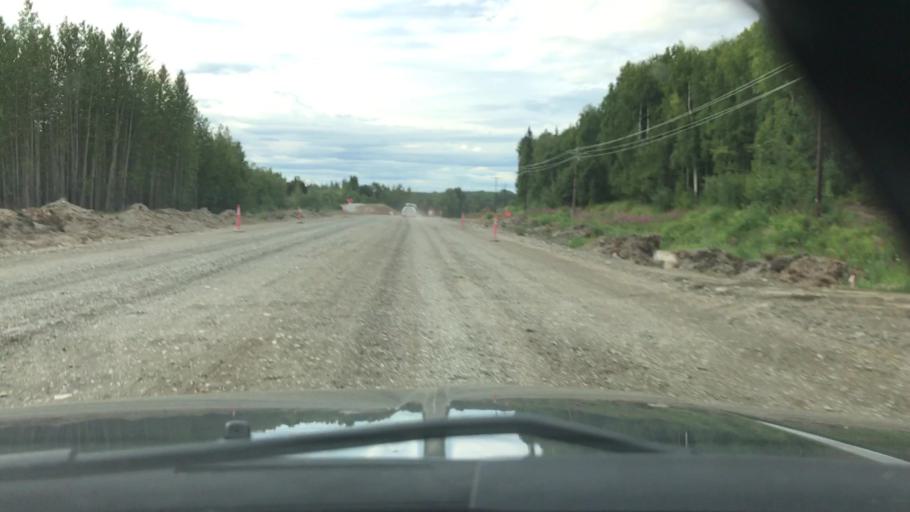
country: US
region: Alaska
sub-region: Matanuska-Susitna Borough
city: Y
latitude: 62.0930
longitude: -150.0618
